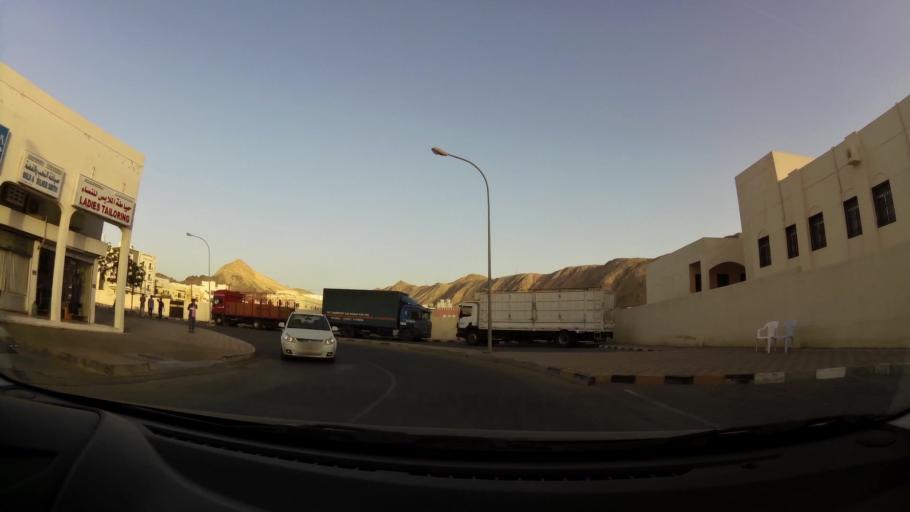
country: OM
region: Muhafazat Masqat
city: Muscat
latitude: 23.5743
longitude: 58.5700
